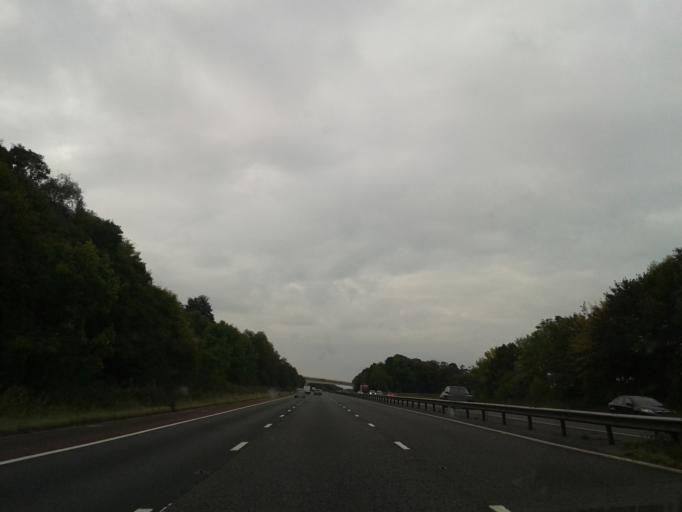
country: GB
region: England
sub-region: Lancashire
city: Bay Horse
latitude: 53.9377
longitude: -2.7565
